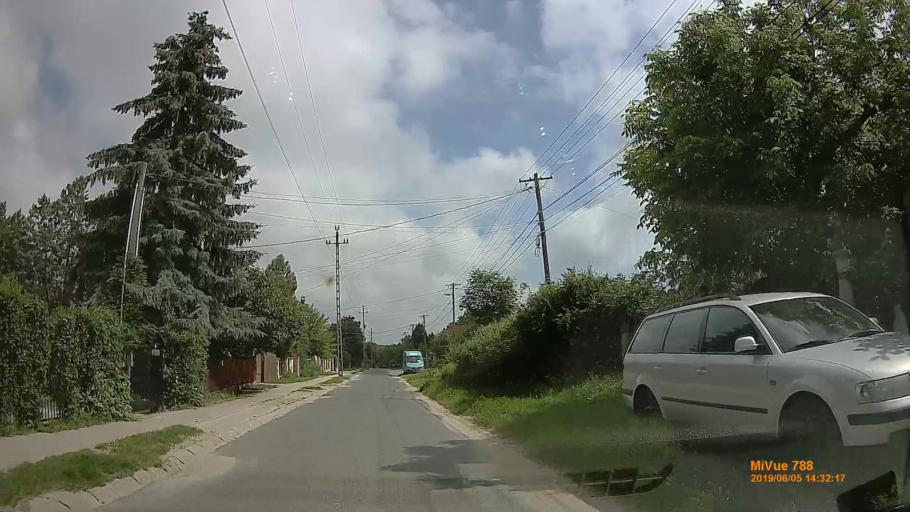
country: HU
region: Pest
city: Kistarcsa
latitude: 47.5565
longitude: 19.2680
